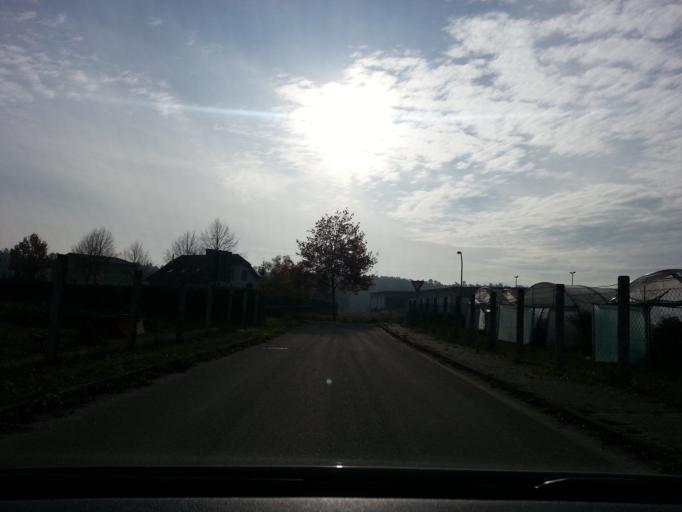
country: DE
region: Mecklenburg-Vorpommern
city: Torgelow
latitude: 53.6311
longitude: 14.0249
